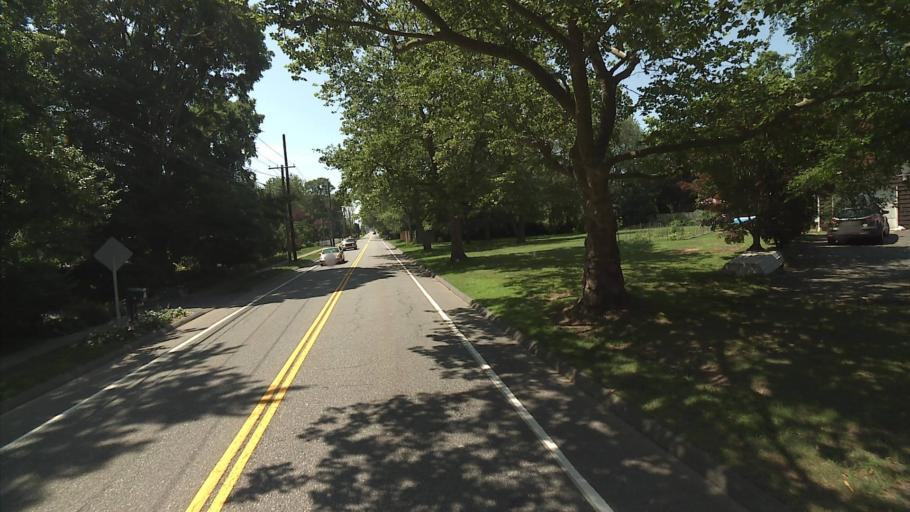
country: US
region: Connecticut
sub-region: Middlesex County
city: Saybrook Manor
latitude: 41.2832
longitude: -72.3912
